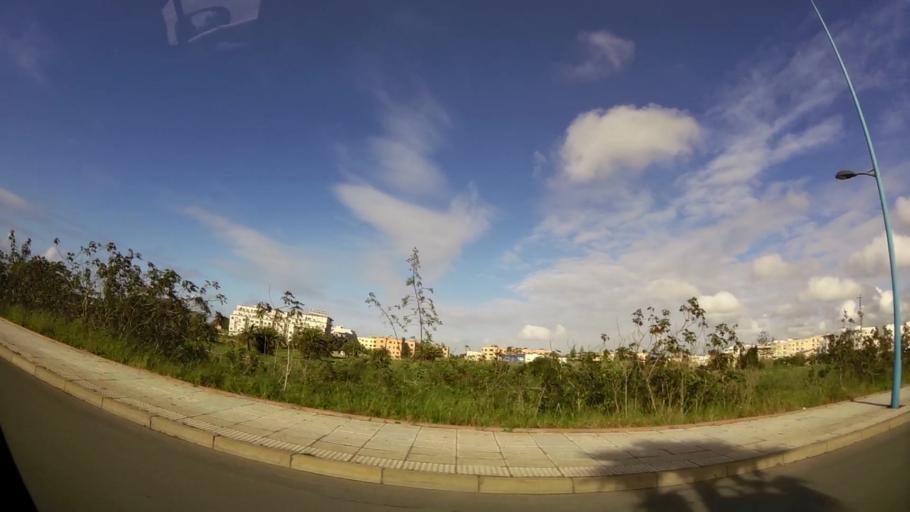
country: MA
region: Grand Casablanca
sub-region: Mohammedia
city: Mohammedia
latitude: 33.7050
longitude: -7.3727
